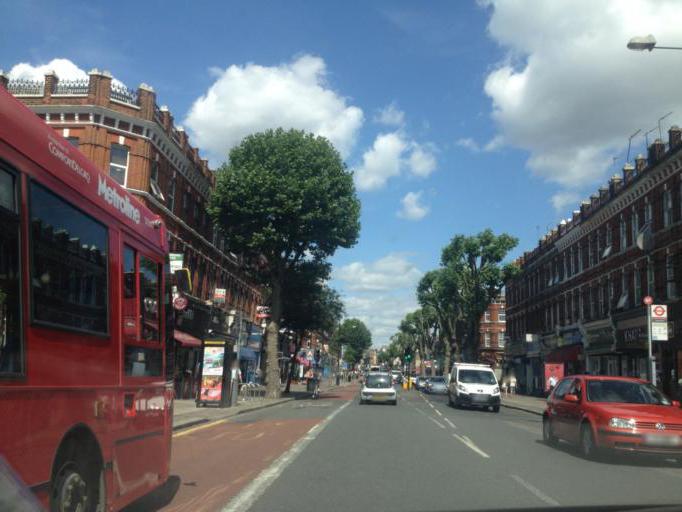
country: GB
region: England
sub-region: Greater London
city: Belsize Park
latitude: 51.5537
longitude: -0.2120
